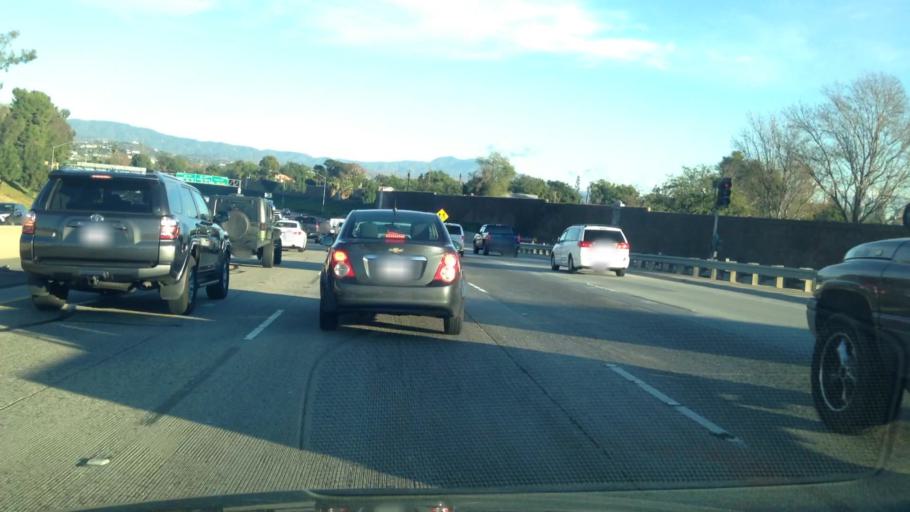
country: US
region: California
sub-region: Orange County
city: Orange
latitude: 33.7753
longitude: -117.8514
